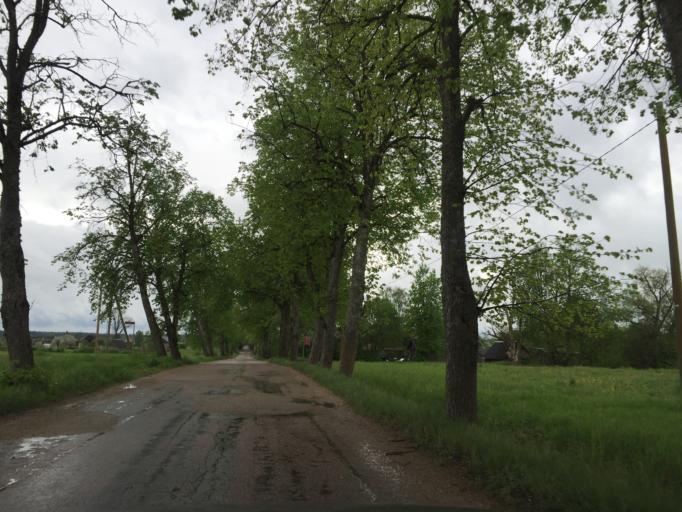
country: LV
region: Ogre
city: Jumprava
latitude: 56.6501
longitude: 24.9271
